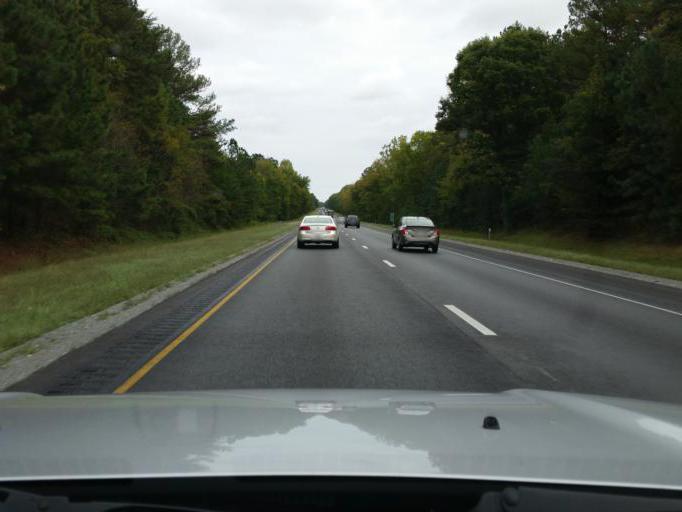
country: US
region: Virginia
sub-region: New Kent County
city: New Kent
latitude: 37.4921
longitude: -77.0000
